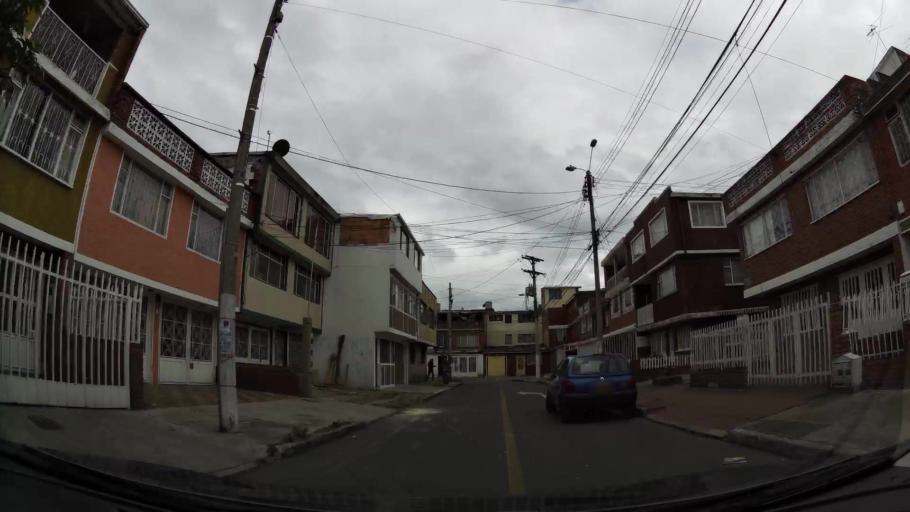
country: CO
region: Bogota D.C.
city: Barrio San Luis
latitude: 4.6870
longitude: -74.0905
